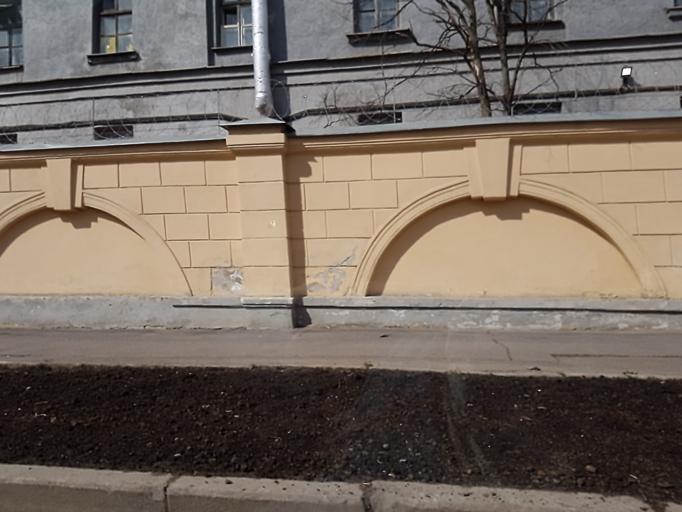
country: RU
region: St.-Petersburg
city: Admiralteisky
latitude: 59.9200
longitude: 30.2756
